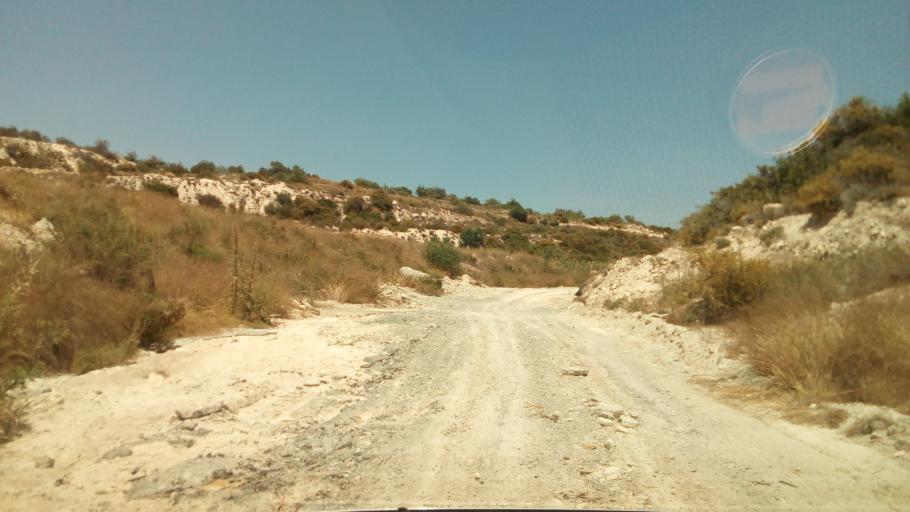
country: CY
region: Limassol
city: Ypsonas
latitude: 34.7240
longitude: 32.9565
